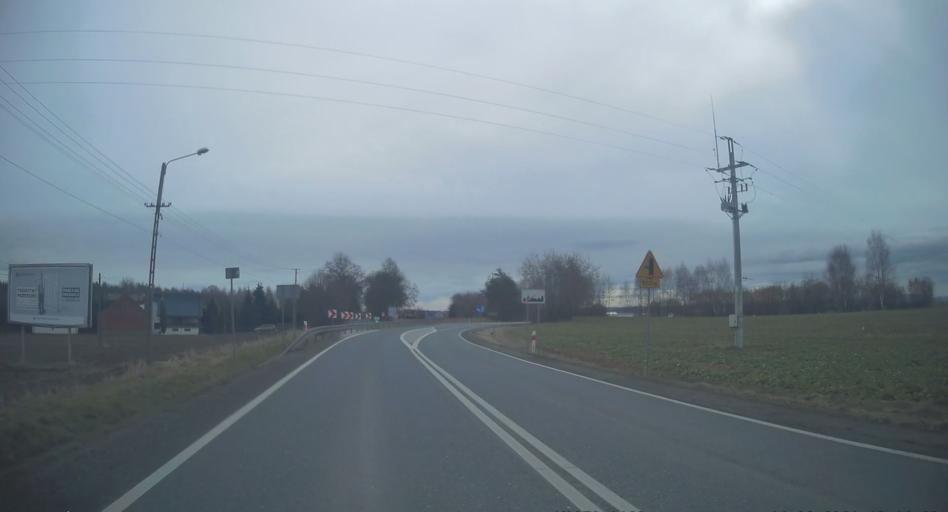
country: PL
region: Lesser Poland Voivodeship
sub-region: Powiat wielicki
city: Szarow
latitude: 50.0005
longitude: 20.2728
